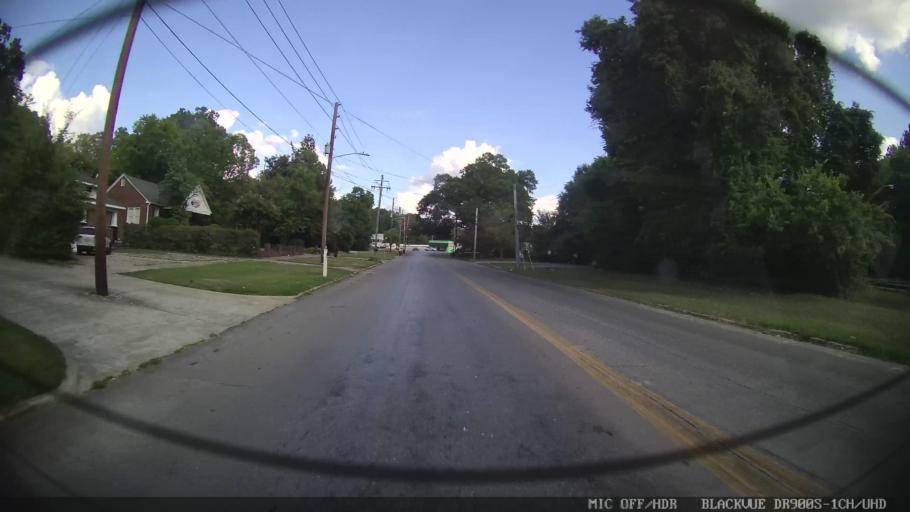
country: US
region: Georgia
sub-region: Floyd County
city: Rome
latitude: 34.2386
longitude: -85.1606
